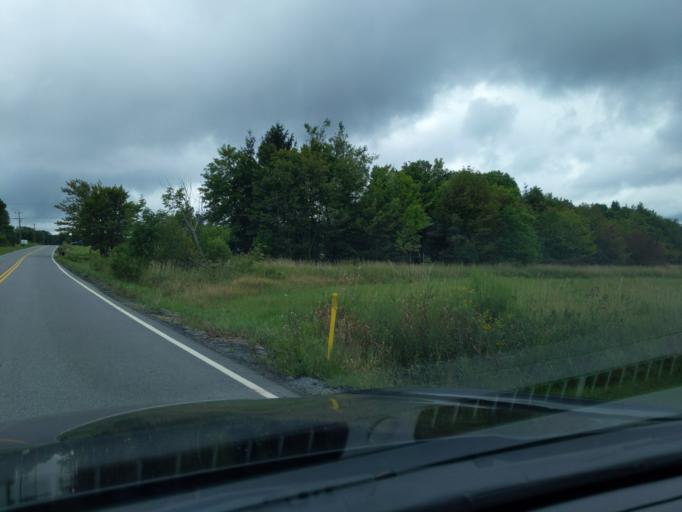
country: US
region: Pennsylvania
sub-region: Blair County
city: Claysburg
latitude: 40.3448
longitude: -78.5549
